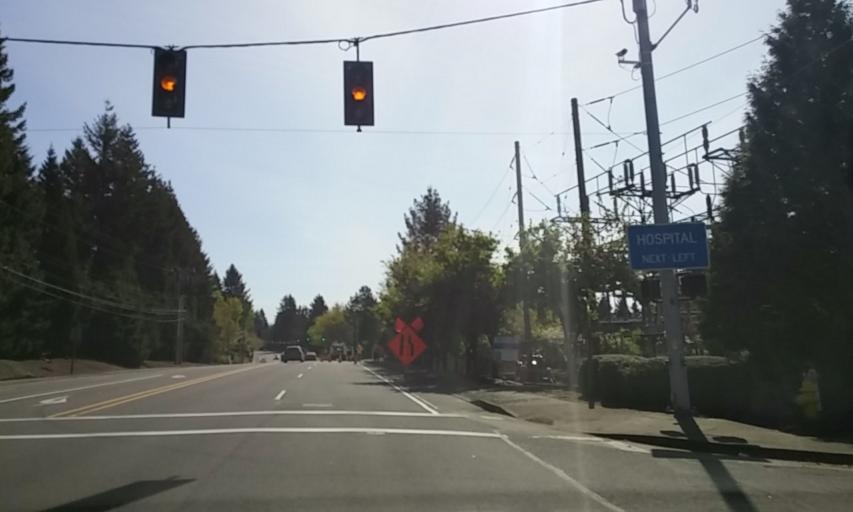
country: US
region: Oregon
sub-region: Washington County
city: West Haven-Sylvan
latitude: 45.5090
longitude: -122.7727
